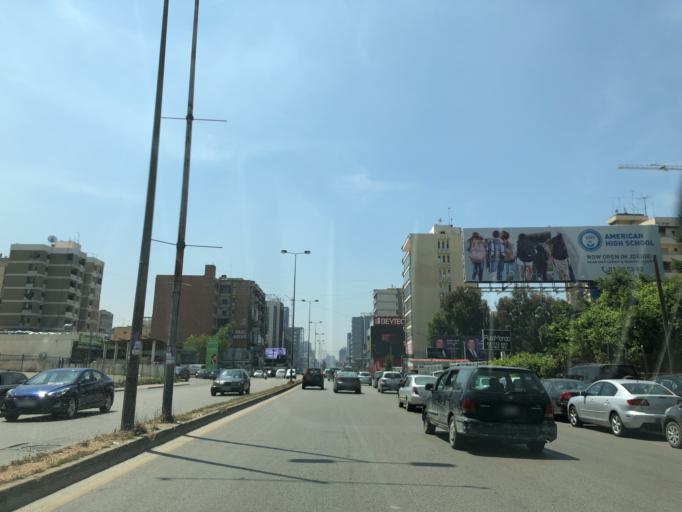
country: LB
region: Mont-Liban
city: Jdaidet el Matn
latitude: 33.8910
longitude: 35.5566
